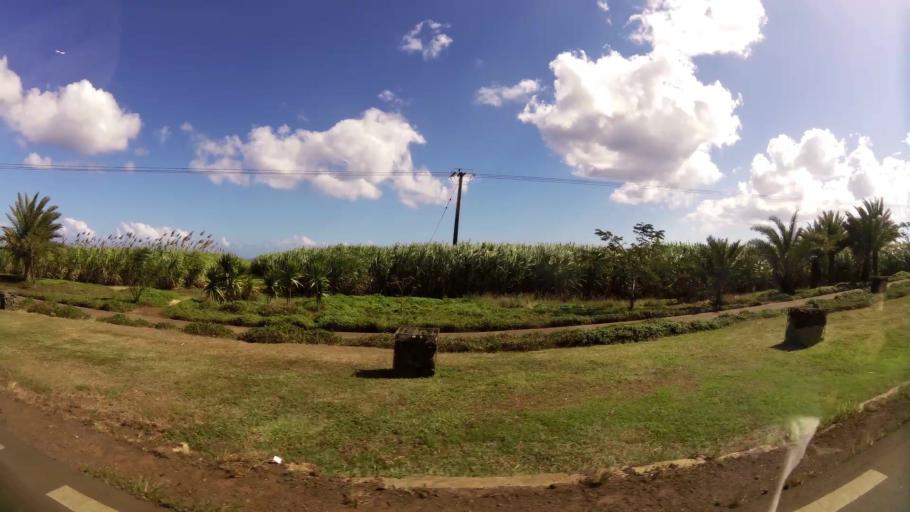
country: MU
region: Black River
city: Cascavelle
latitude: -20.2698
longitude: 57.4061
